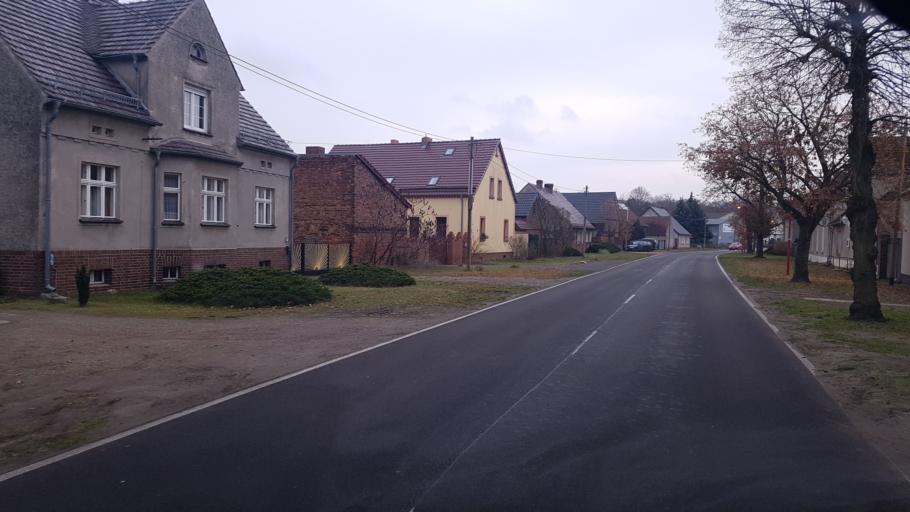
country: DE
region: Brandenburg
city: Schenkendobern
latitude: 51.9595
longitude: 14.6338
